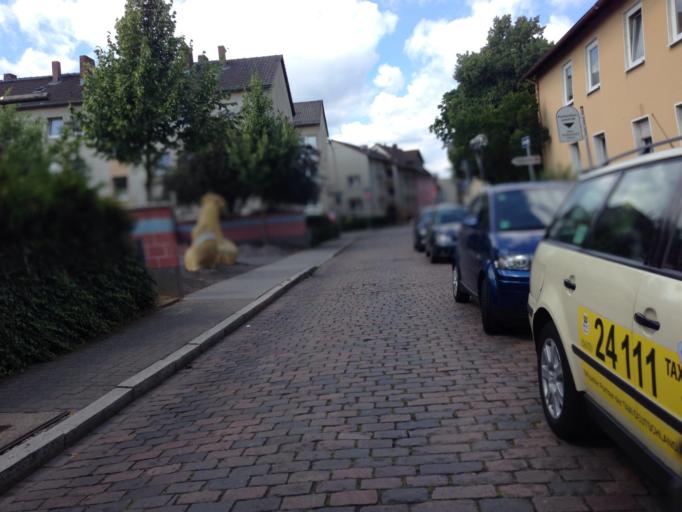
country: DE
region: Hesse
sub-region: Regierungsbezirk Darmstadt
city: Hanau am Main
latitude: 50.1302
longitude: 8.9178
